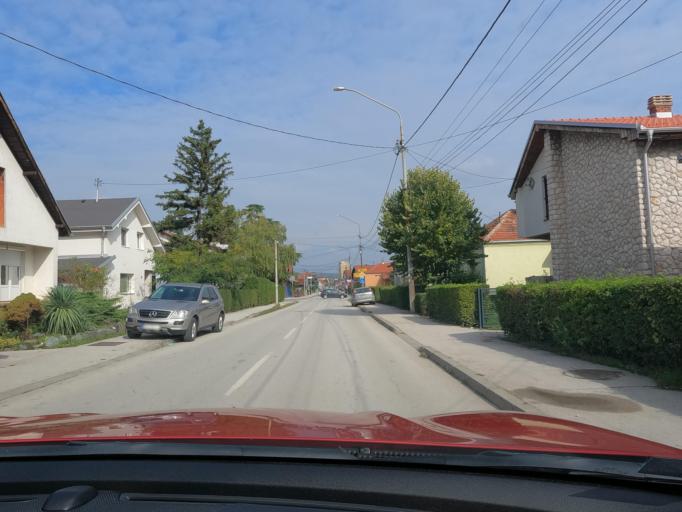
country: RS
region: Central Serbia
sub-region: Moravicki Okrug
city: Cacak
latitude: 43.8811
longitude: 20.3392
